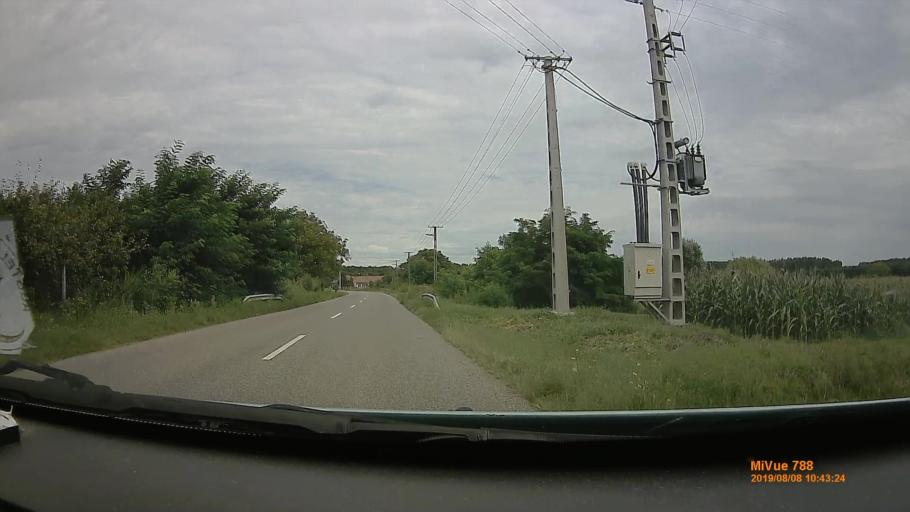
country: HU
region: Hajdu-Bihar
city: Nyiradony
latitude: 47.7218
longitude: 21.8770
